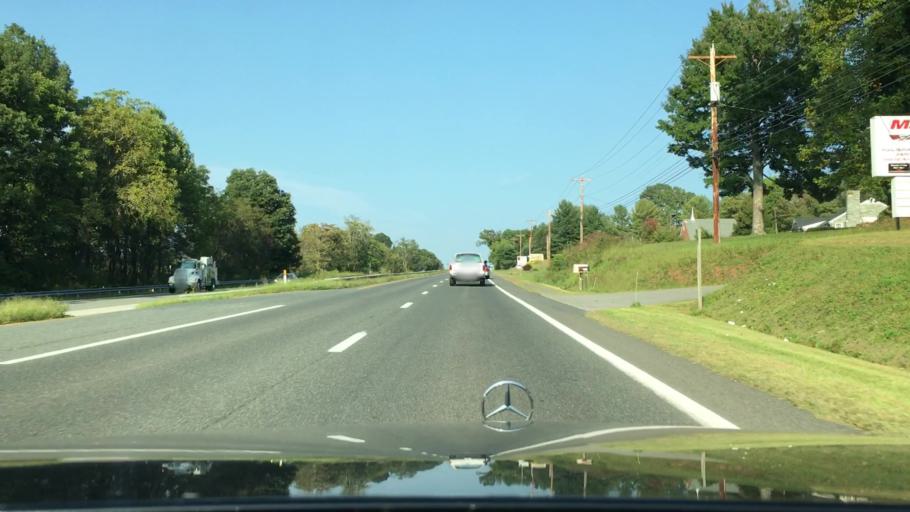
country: US
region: Virginia
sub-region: Amherst County
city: Amherst
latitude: 37.5262
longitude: -79.1104
